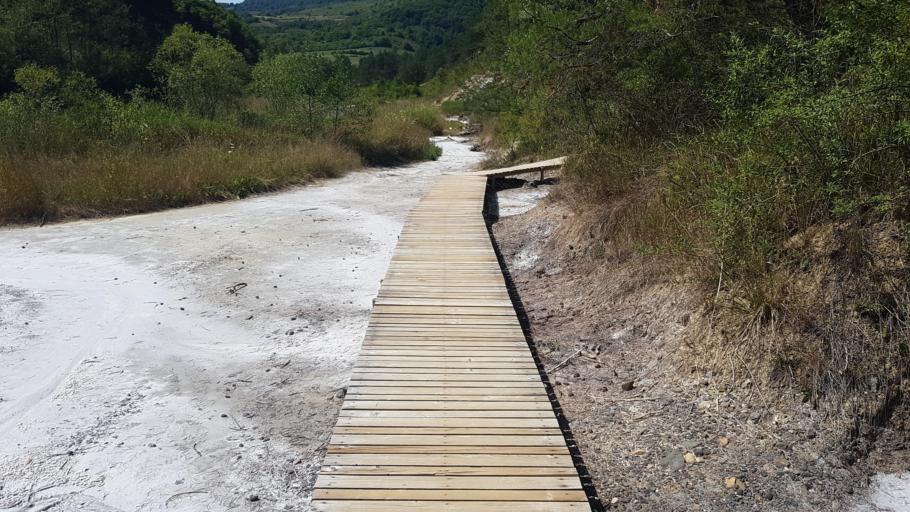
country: RO
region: Harghita
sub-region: Comuna Praid
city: Praid
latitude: 46.5418
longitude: 25.1201
